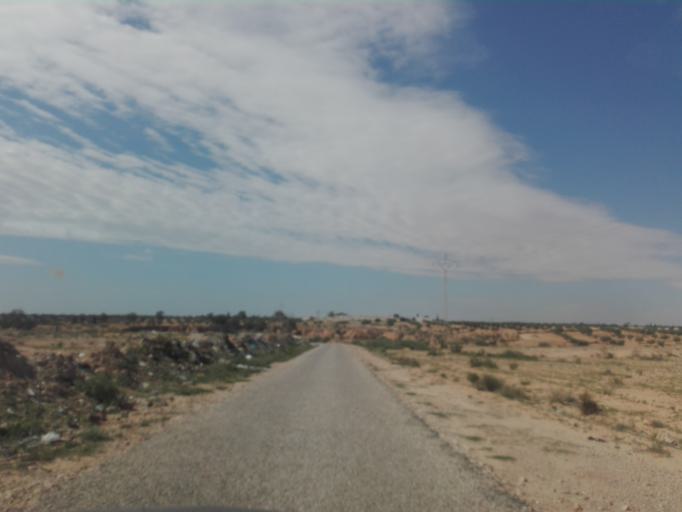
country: TN
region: Safaqis
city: Sfax
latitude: 34.6892
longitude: 10.5624
